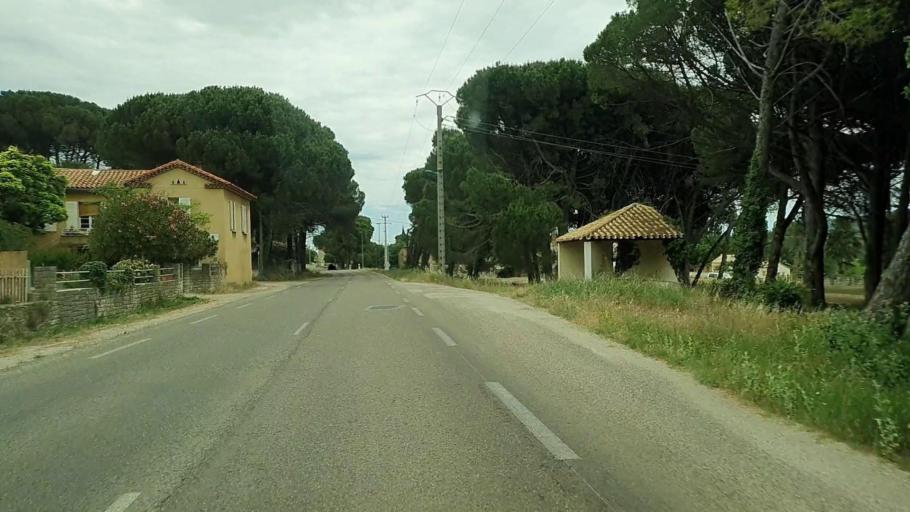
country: FR
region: Languedoc-Roussillon
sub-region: Departement du Gard
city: Tresques
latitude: 44.1216
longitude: 4.5978
